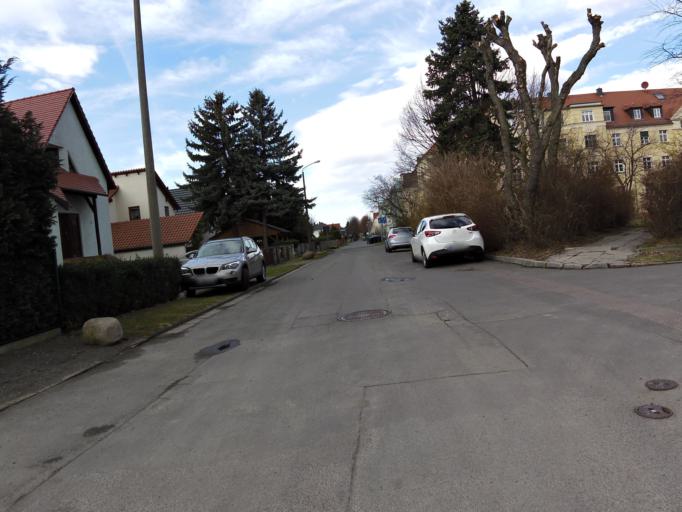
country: DE
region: Saxony
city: Taucha
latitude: 51.3333
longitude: 12.4775
